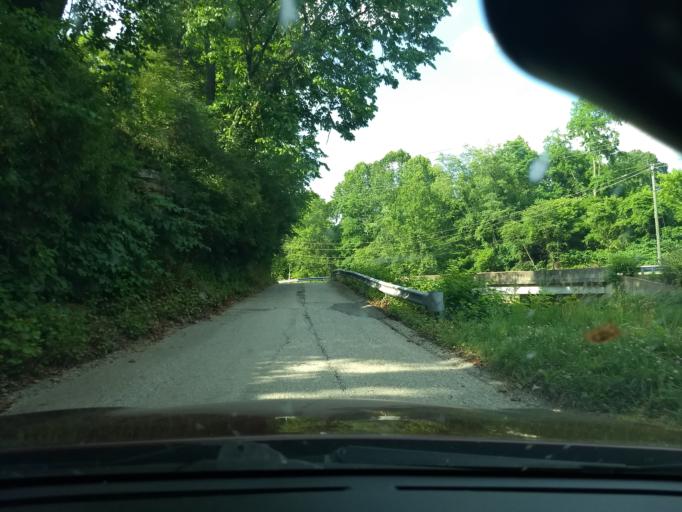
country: US
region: Pennsylvania
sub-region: Westmoreland County
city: Irwin
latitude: 40.3378
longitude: -79.7187
